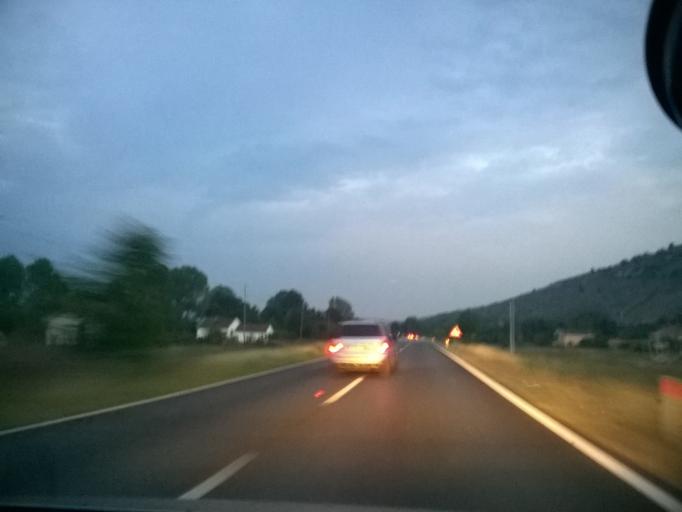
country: ME
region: Danilovgrad
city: Danilovgrad
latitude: 42.5105
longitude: 19.1303
